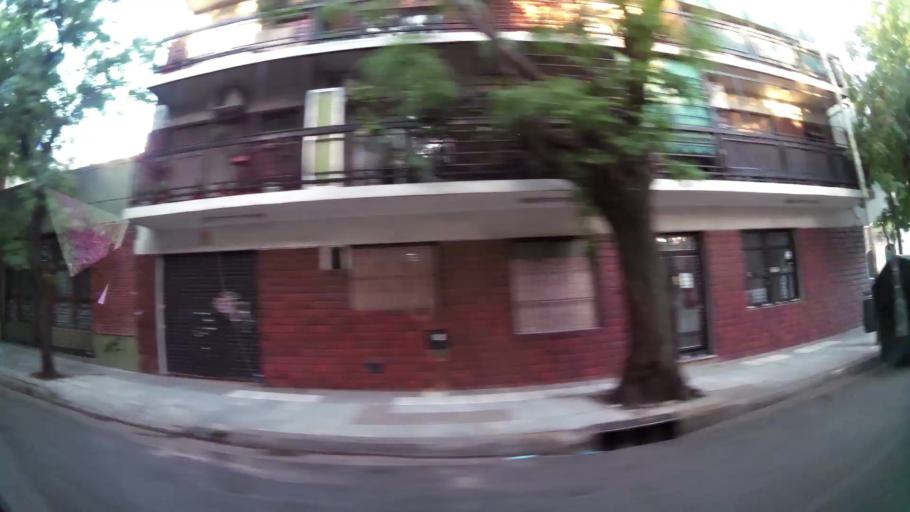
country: AR
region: Buenos Aires F.D.
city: Buenos Aires
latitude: -34.6328
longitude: -58.4096
